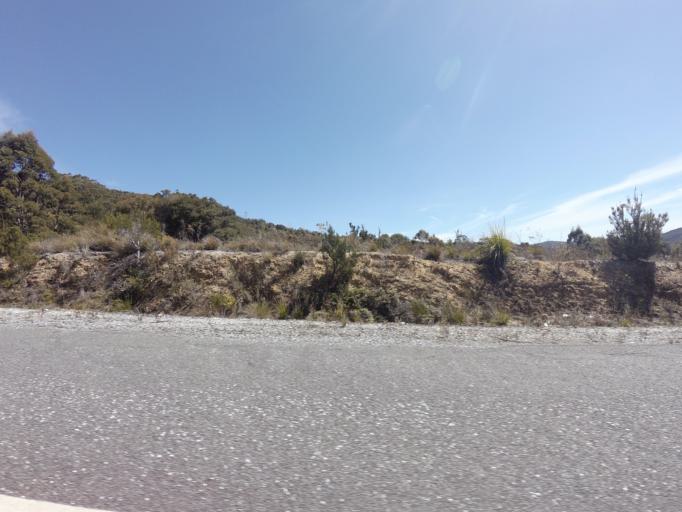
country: AU
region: Tasmania
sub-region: West Coast
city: Queenstown
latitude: -42.7911
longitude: 146.0631
